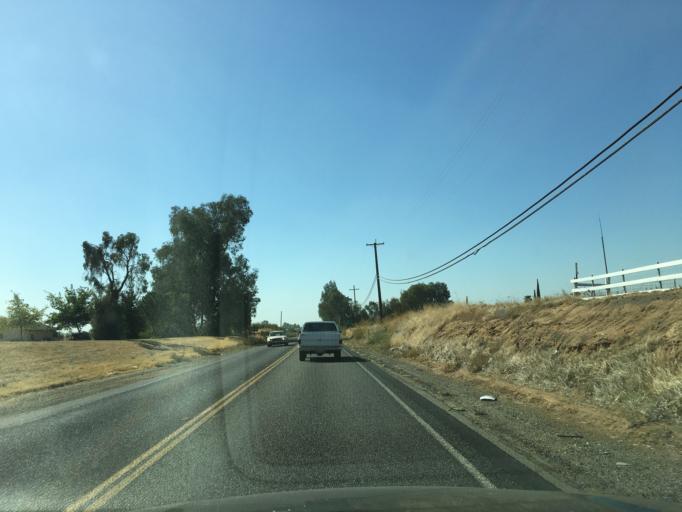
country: US
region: California
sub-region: Madera County
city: Parksdale
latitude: 36.9956
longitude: -119.9913
